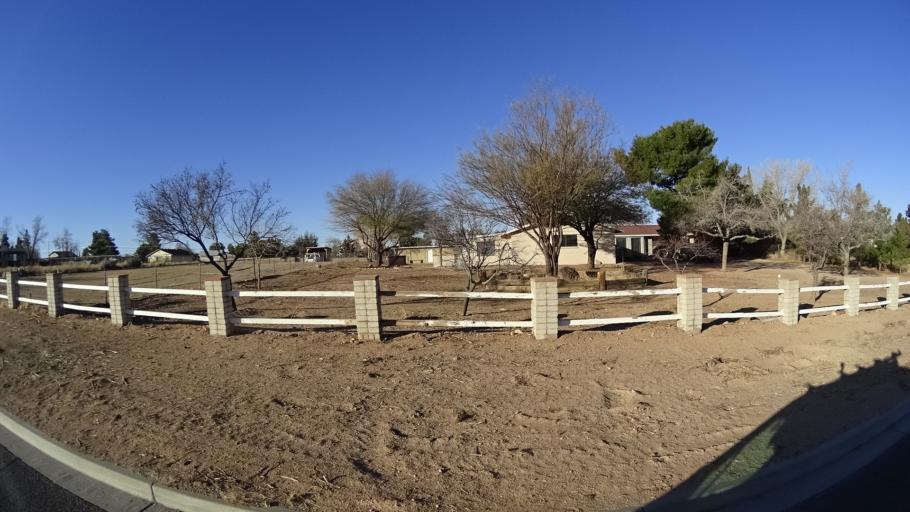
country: US
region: Arizona
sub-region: Mohave County
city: Kingman
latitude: 35.2011
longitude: -114.0058
